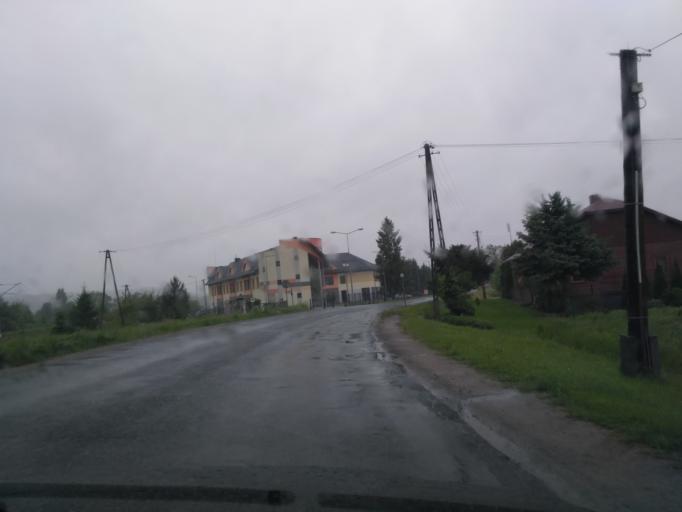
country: PL
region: Lesser Poland Voivodeship
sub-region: Powiat gorlicki
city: Gorlice
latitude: 49.6824
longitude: 21.1852
